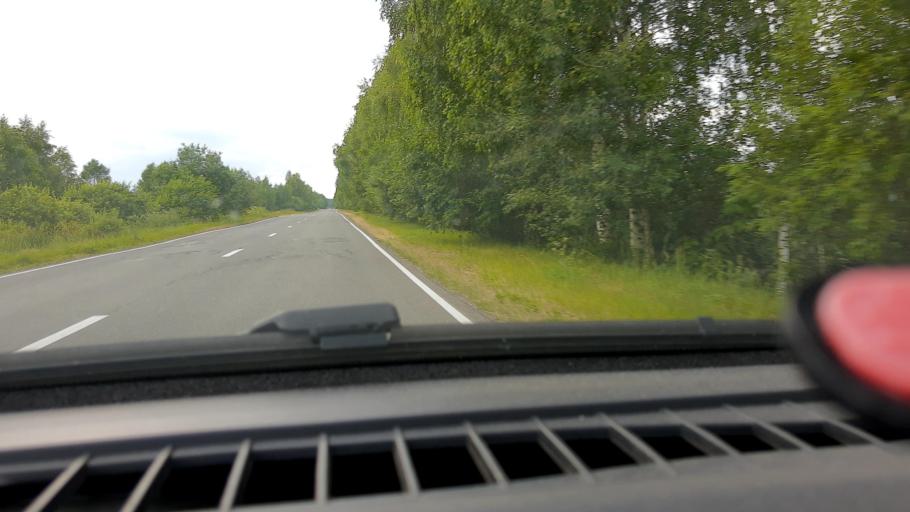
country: RU
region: Nizjnij Novgorod
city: Neklyudovo
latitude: 56.5251
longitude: 43.8600
